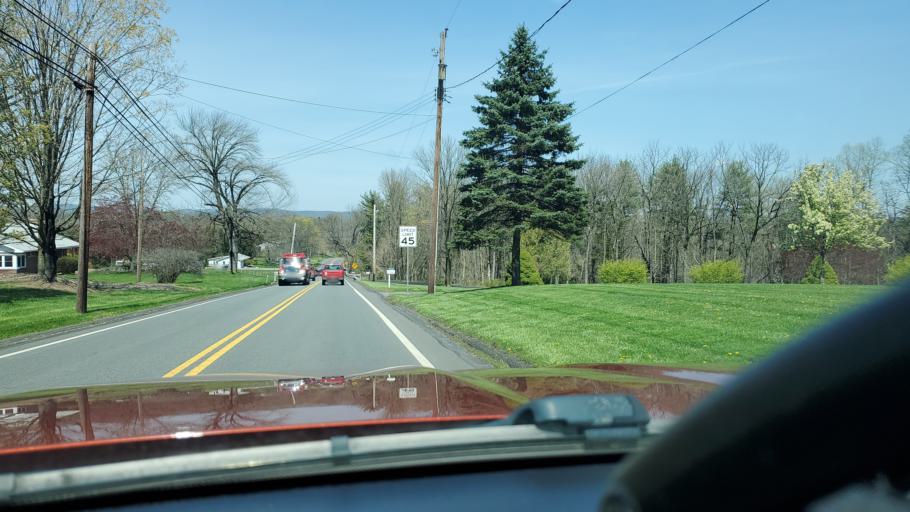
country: US
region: Pennsylvania
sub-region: Montgomery County
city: Pennsburg
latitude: 40.3678
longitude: -75.5220
